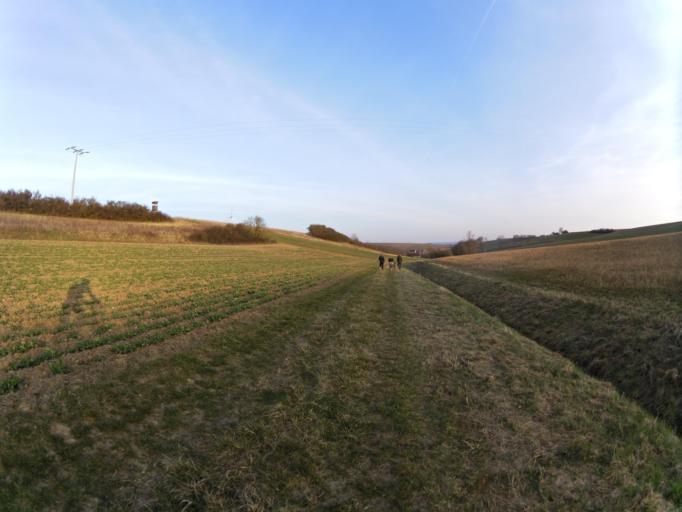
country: DE
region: Bavaria
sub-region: Regierungsbezirk Unterfranken
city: Prosselsheim
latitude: 49.8343
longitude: 10.1401
